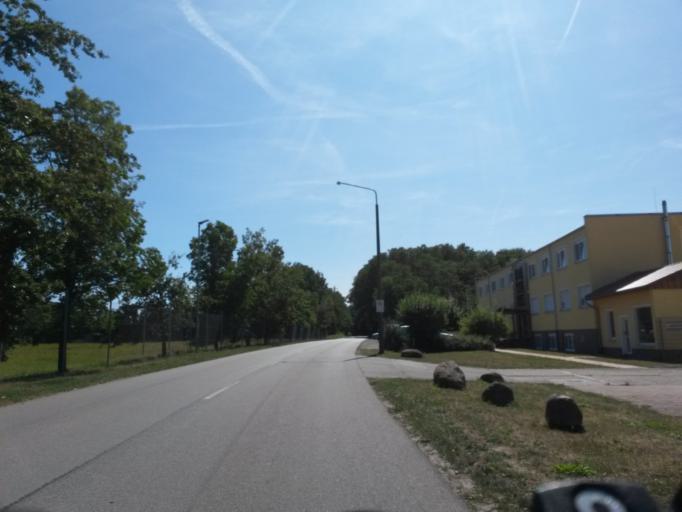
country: DE
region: Saxony-Anhalt
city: Tangermunde
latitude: 52.5614
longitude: 11.9721
